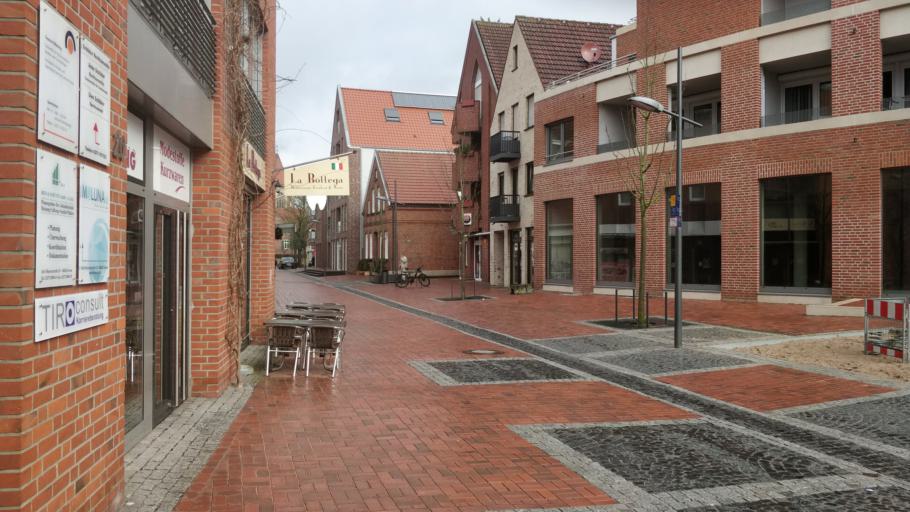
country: DE
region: North Rhine-Westphalia
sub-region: Regierungsbezirk Munster
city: Greven
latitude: 52.0909
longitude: 7.6132
